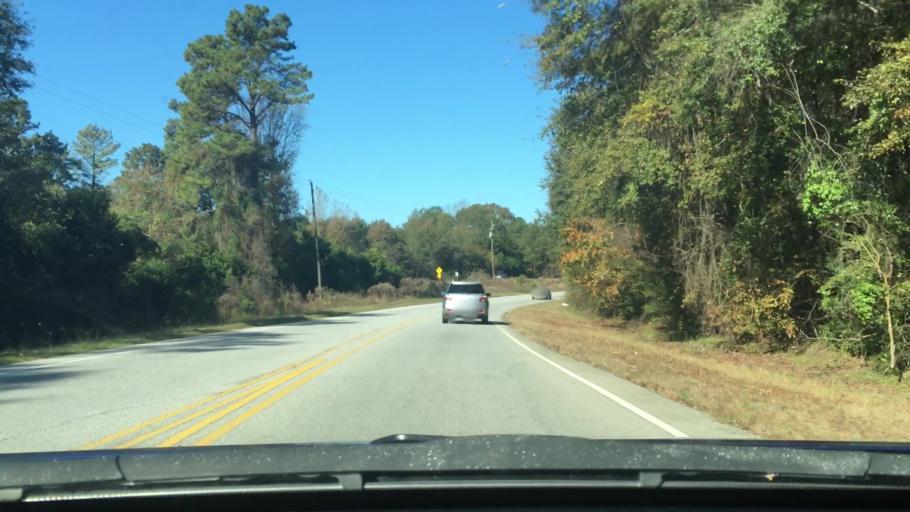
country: US
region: South Carolina
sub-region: Sumter County
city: Lakewood
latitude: 33.8733
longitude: -80.3662
